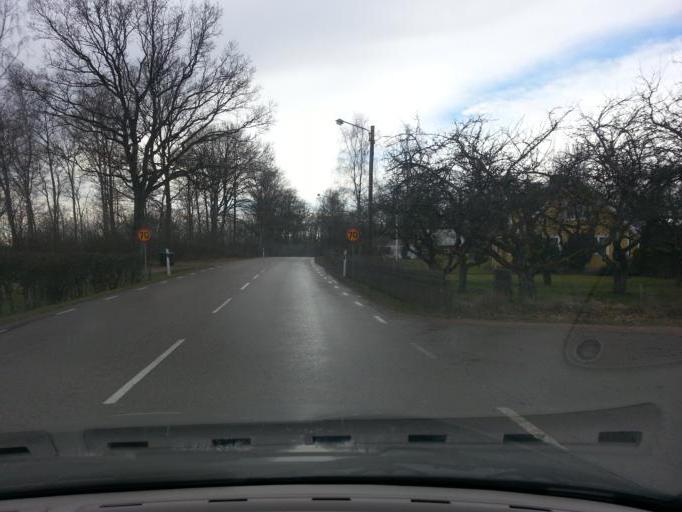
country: SE
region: Skane
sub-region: Klippans Kommun
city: Ljungbyhed
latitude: 56.0791
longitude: 13.2583
